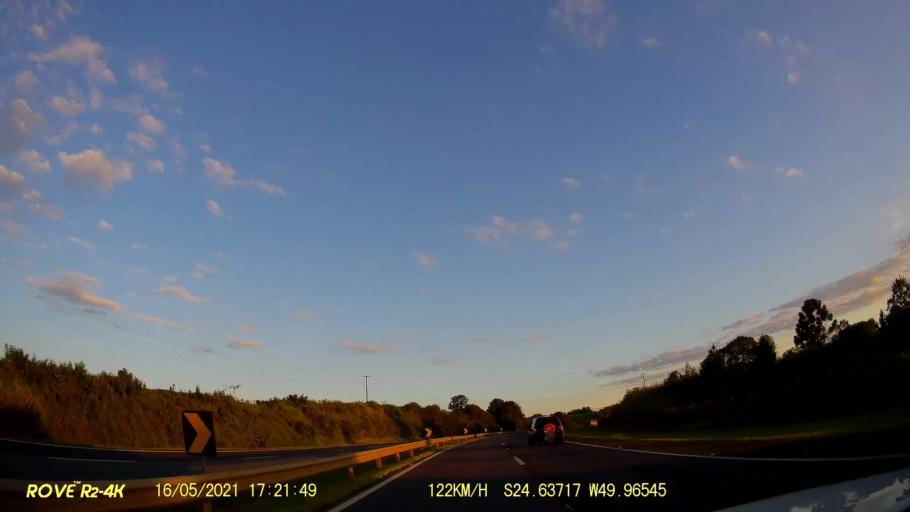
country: BR
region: Parana
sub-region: Pirai Do Sul
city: Pirai do Sul
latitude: -24.6376
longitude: -49.9654
